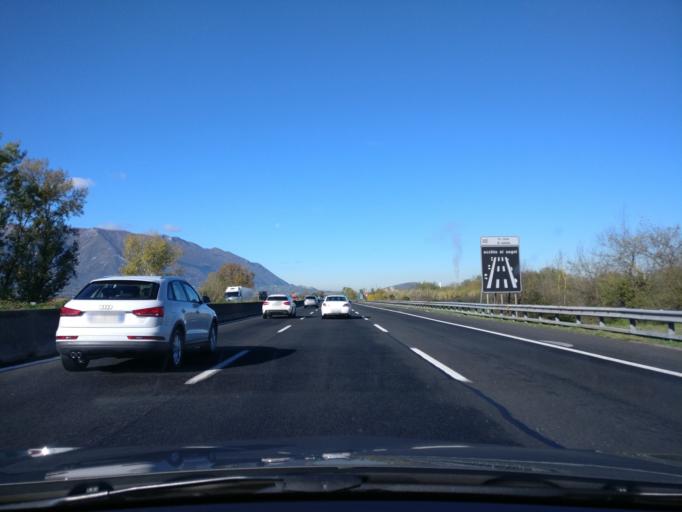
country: IT
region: Latium
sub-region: Provincia di Frosinone
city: Frosinone
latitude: 41.6280
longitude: 13.2888
